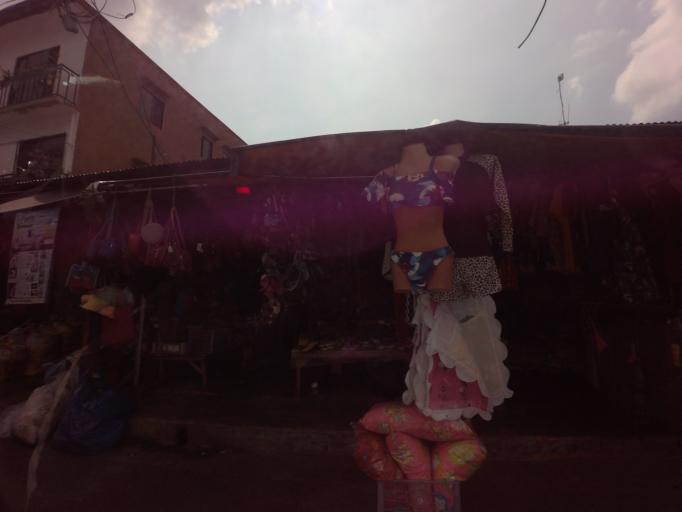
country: PH
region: Metro Manila
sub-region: Makati City
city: Makati City
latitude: 14.5701
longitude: 121.0203
